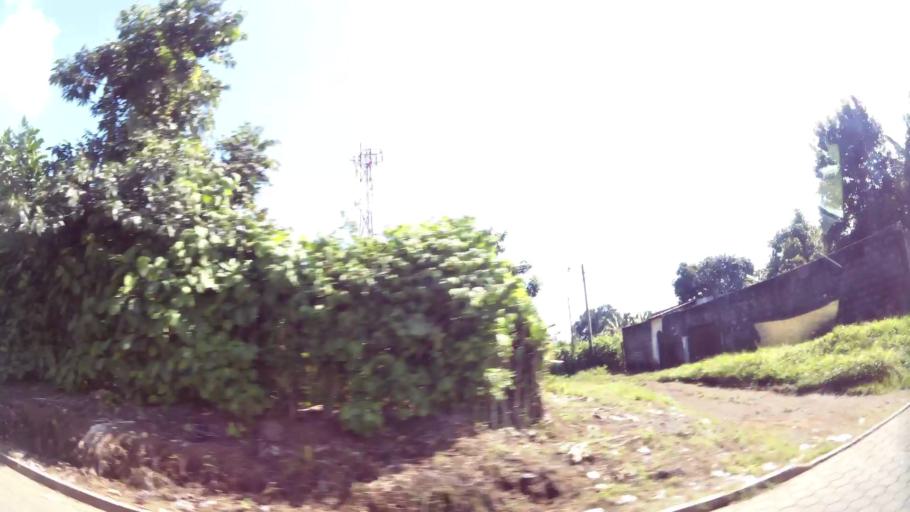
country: GT
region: Suchitepeque
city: Mazatenango
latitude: 14.5312
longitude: -91.4853
